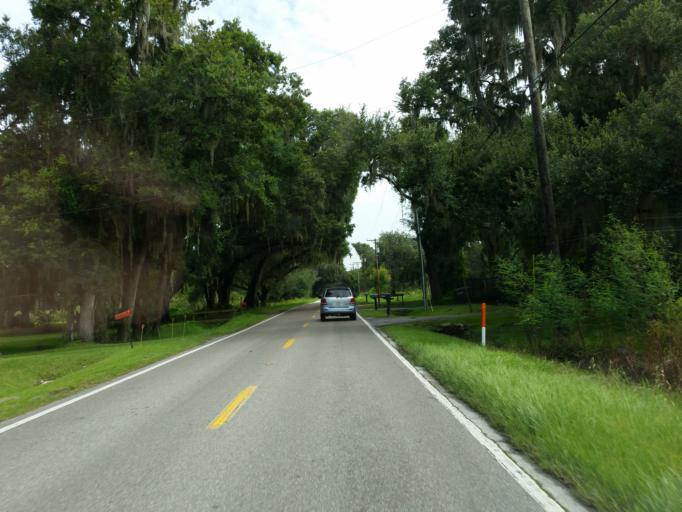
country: US
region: Florida
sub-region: Hillsborough County
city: Seffner
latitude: 27.9774
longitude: -82.2529
